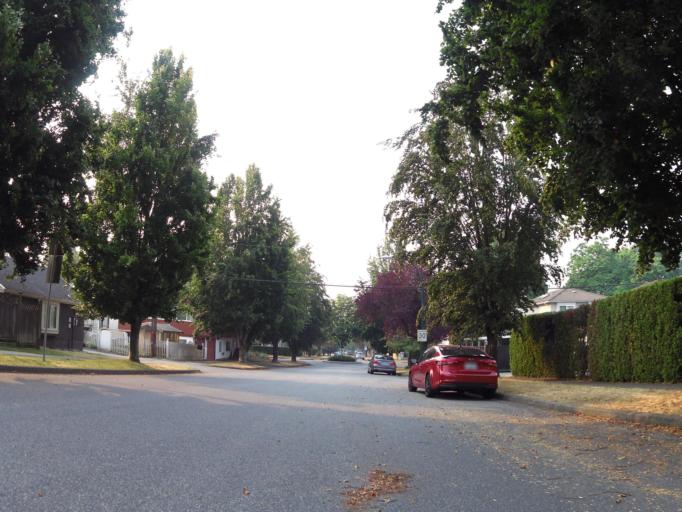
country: CA
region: British Columbia
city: Richmond
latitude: 49.2130
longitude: -123.1436
